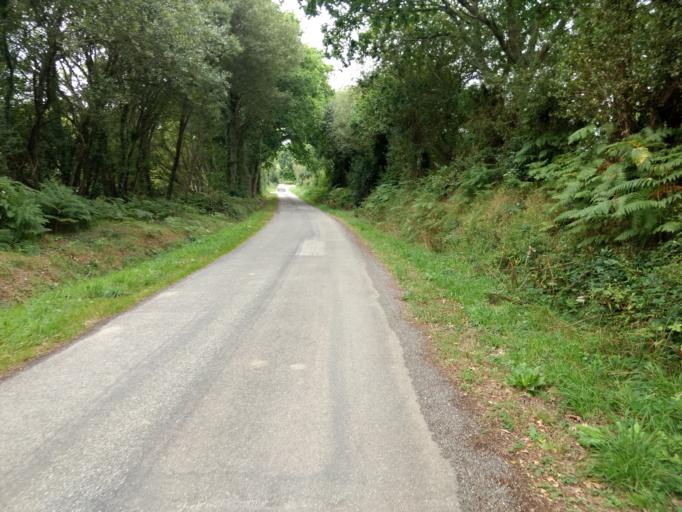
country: FR
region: Brittany
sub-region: Departement du Finistere
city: Loperhet
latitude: 48.3580
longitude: -4.3008
